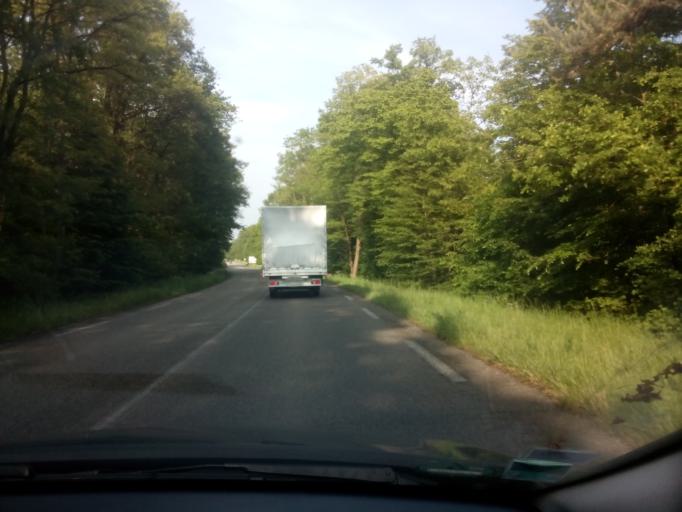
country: FR
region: Alsace
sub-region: Departement du Bas-Rhin
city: Haguenau
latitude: 48.8285
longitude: 7.8183
